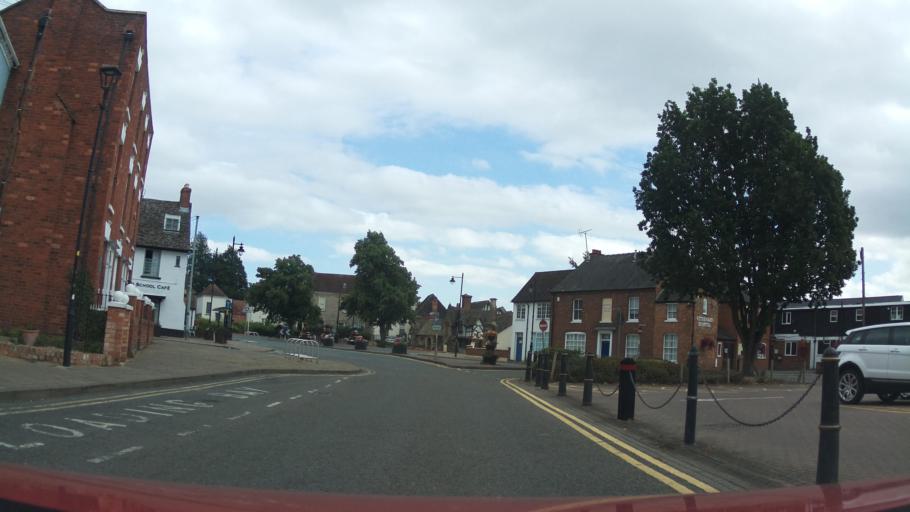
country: GB
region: England
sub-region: Worcestershire
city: Evesham
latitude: 52.0920
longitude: -1.9508
